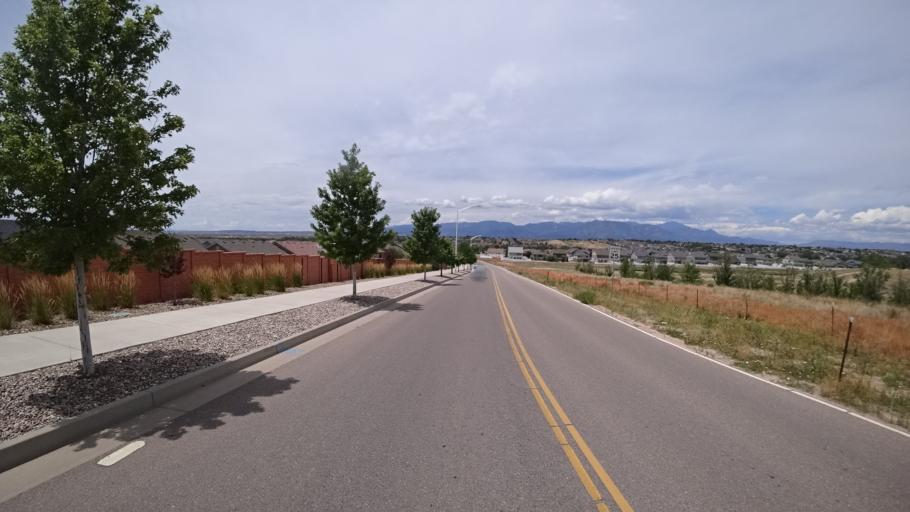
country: US
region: Colorado
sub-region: El Paso County
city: Fountain
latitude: 38.6939
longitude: -104.6749
